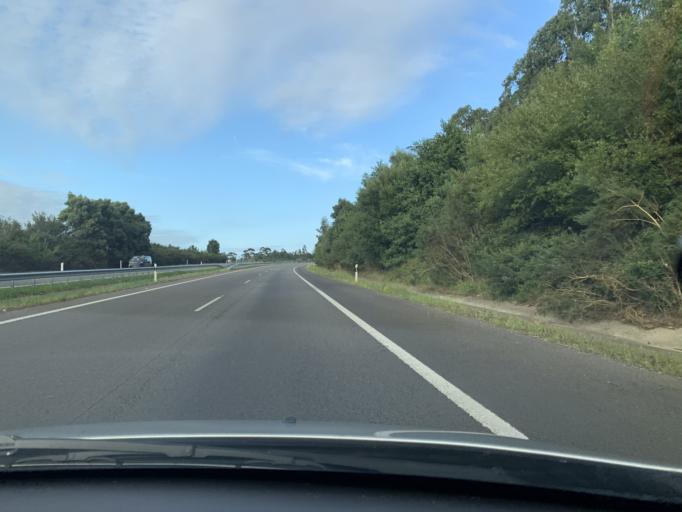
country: ES
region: Galicia
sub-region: Provincia de Lugo
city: Barreiros
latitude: 43.5369
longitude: -7.1933
